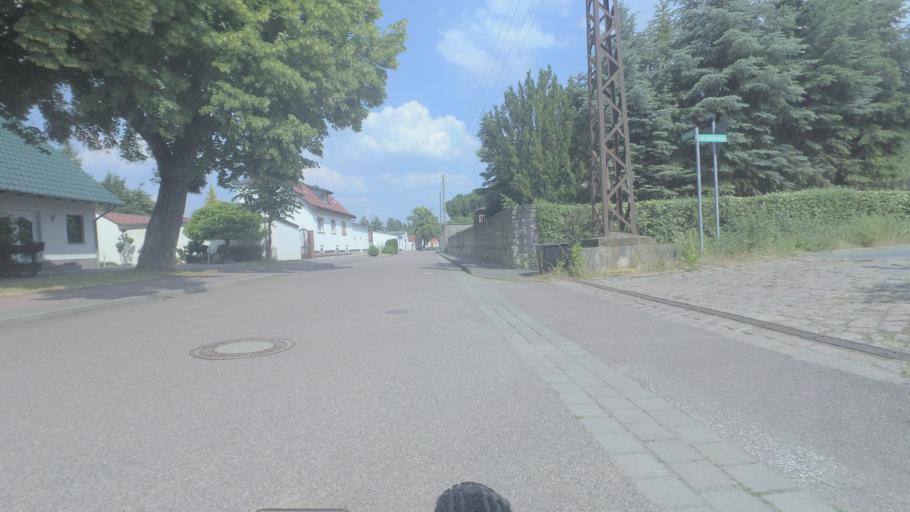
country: DE
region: Saxony-Anhalt
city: Koethen
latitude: 51.7616
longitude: 11.9361
